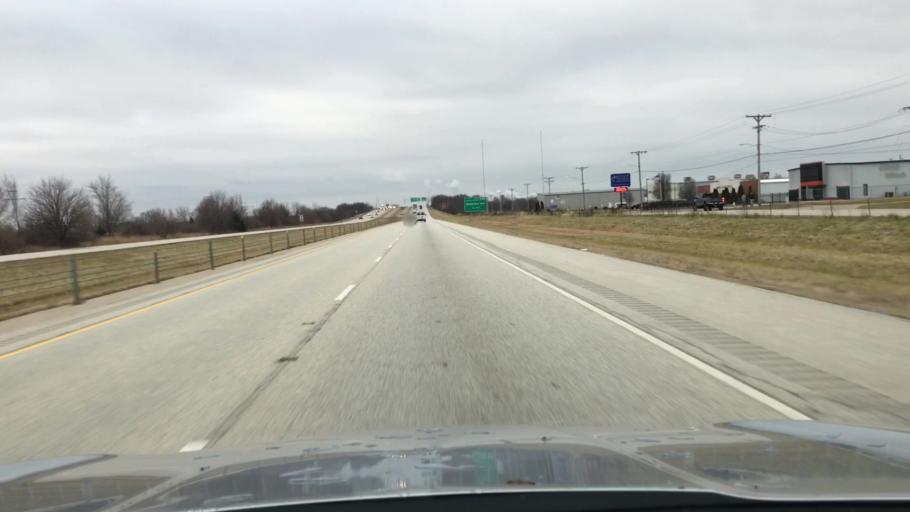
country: US
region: Illinois
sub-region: Sangamon County
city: Grandview
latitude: 39.8428
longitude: -89.5942
